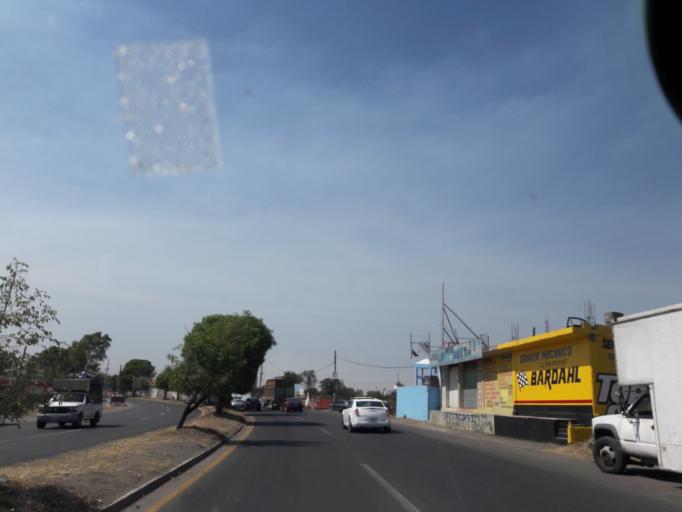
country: MX
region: Tlaxcala
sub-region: Teolocholco
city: Teolocholco
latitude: 19.2493
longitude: -98.1957
